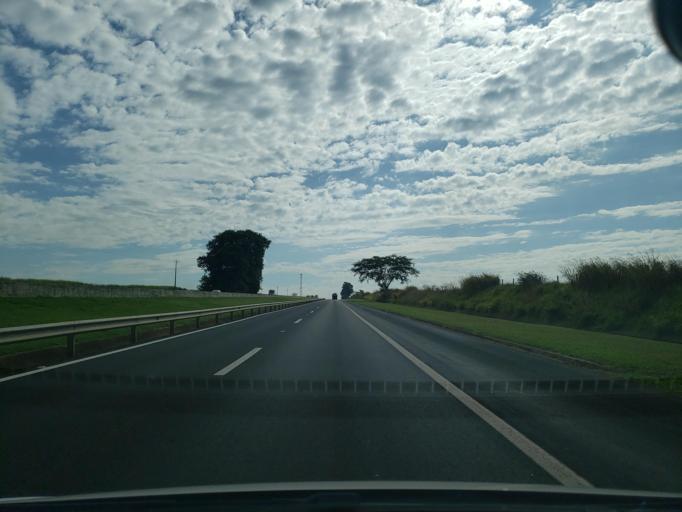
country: BR
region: Sao Paulo
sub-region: Lins
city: Lins
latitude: -21.6414
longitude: -49.8247
